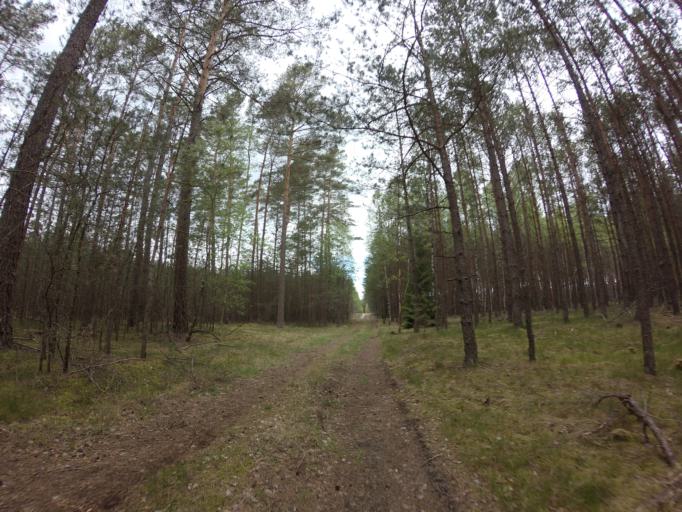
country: PL
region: West Pomeranian Voivodeship
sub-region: Powiat drawski
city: Kalisz Pomorski
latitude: 53.1904
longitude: 16.0036
